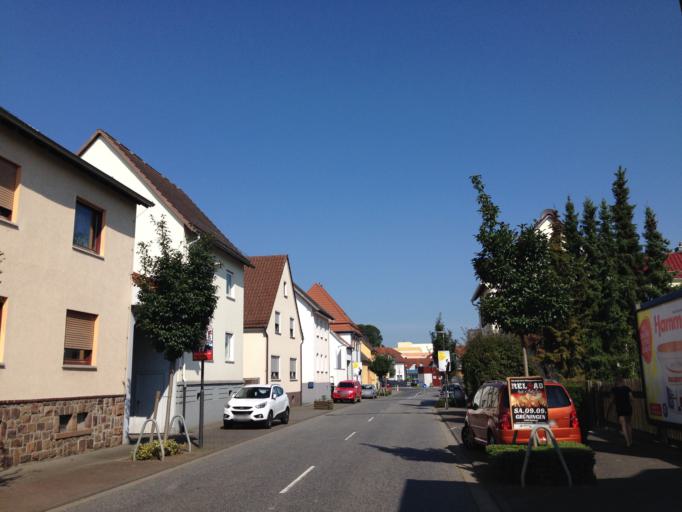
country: DE
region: Hesse
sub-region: Regierungsbezirk Giessen
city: Langgons
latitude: 50.5269
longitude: 8.6741
